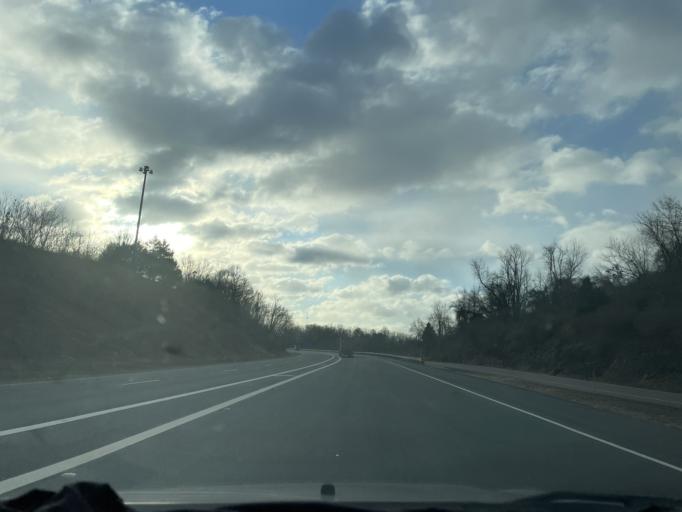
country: US
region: Maryland
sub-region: Washington County
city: Hancock
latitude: 39.7106
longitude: -78.1874
